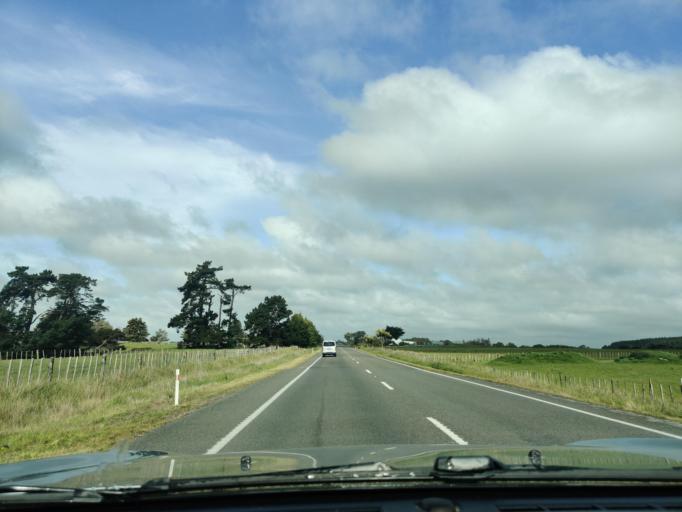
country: NZ
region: Manawatu-Wanganui
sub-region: Rangitikei District
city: Bulls
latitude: -40.0776
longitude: 175.2382
